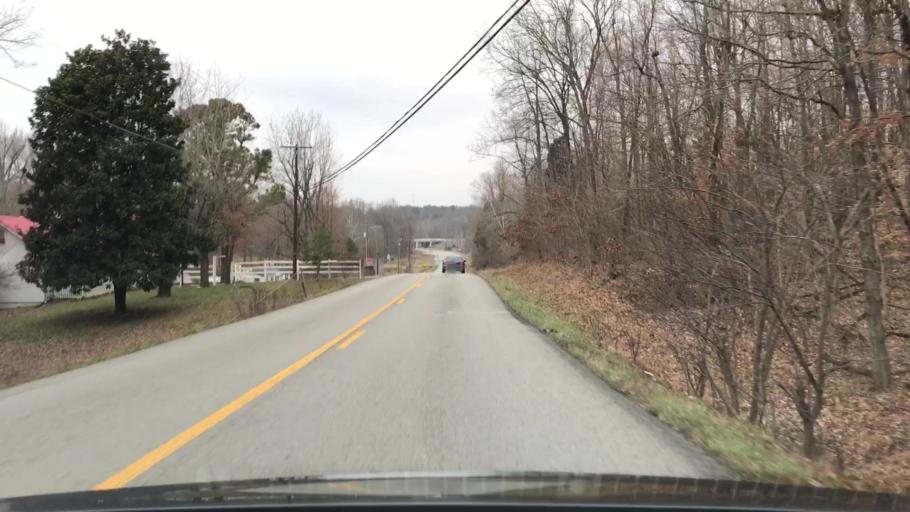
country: US
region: Kentucky
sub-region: Muhlenberg County
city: Morehead
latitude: 37.2468
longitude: -87.1955
